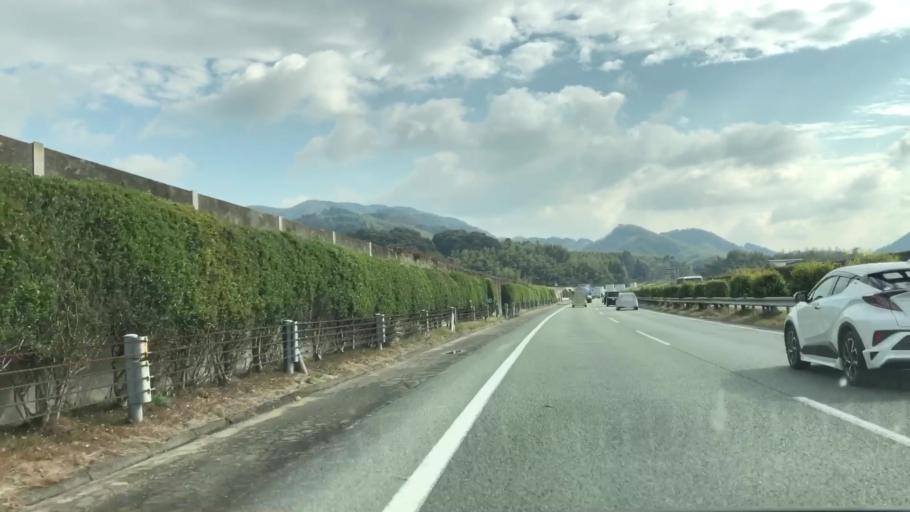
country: JP
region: Fukuoka
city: Setakamachi-takayanagi
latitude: 33.1150
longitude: 130.5290
